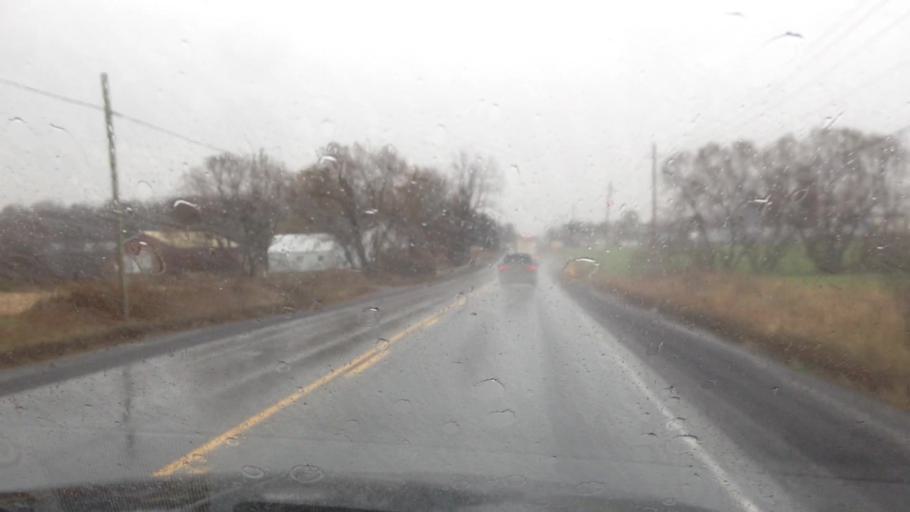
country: CA
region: Ontario
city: Bourget
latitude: 45.2789
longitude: -75.3160
